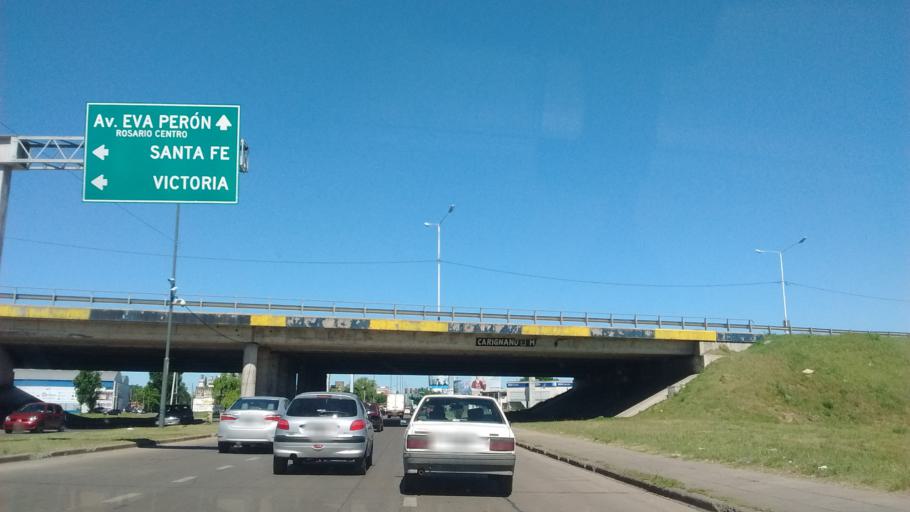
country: AR
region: Santa Fe
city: Granadero Baigorria
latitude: -32.9311
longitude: -60.7240
